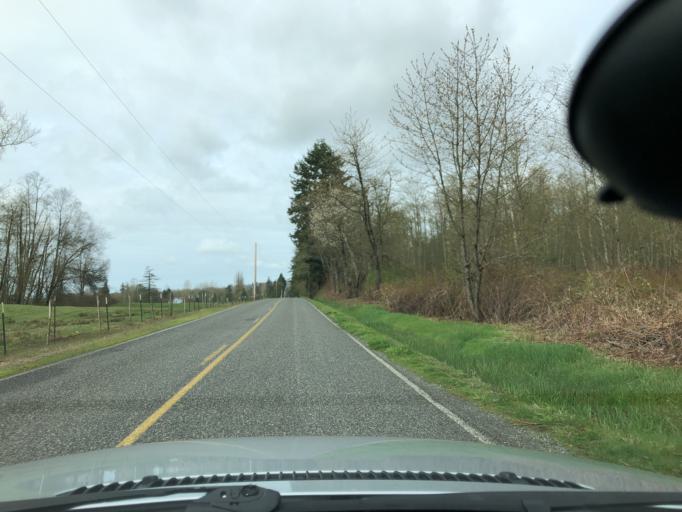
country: CA
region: British Columbia
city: Langley
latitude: 48.9792
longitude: -122.5868
